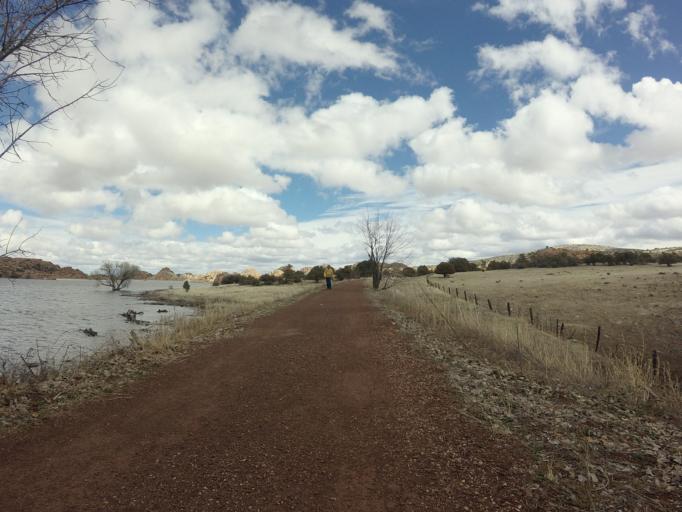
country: US
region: Arizona
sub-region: Yavapai County
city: Prescott
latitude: 34.5845
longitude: -112.4187
